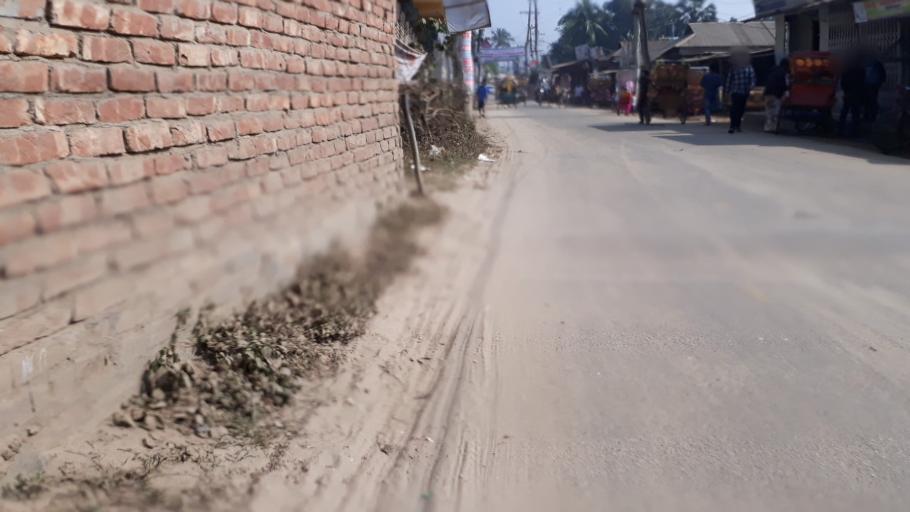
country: BD
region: Dhaka
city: Tungi
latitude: 23.8481
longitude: 90.2690
